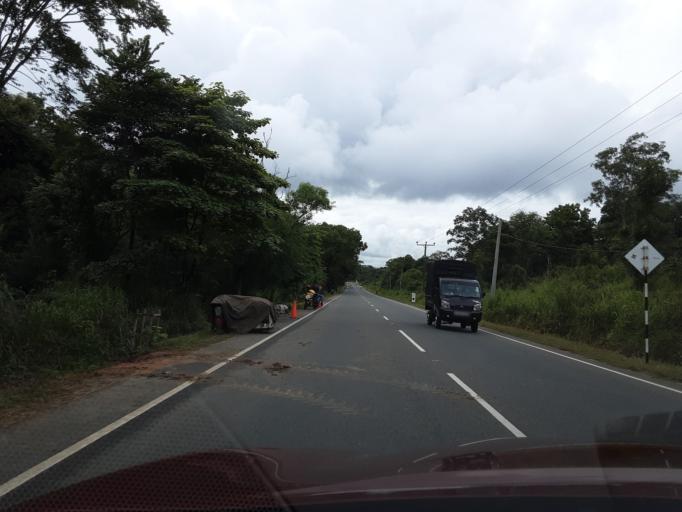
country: LK
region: Uva
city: Badulla
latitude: 7.3986
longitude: 81.1072
